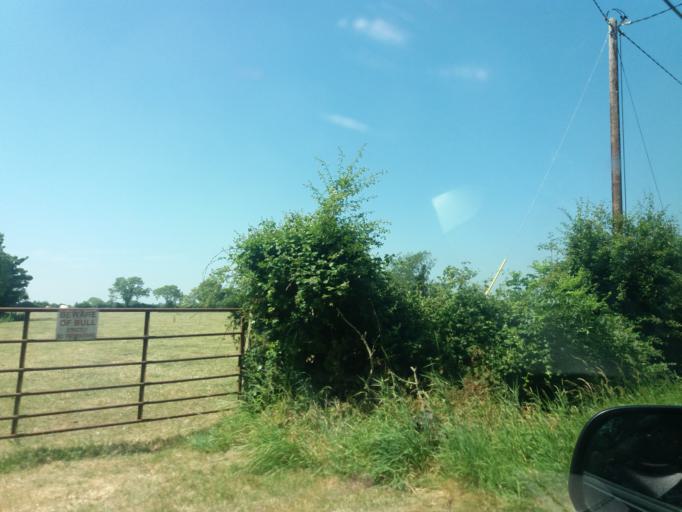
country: IE
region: Leinster
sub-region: Fingal County
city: Swords
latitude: 53.5284
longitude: -6.2359
